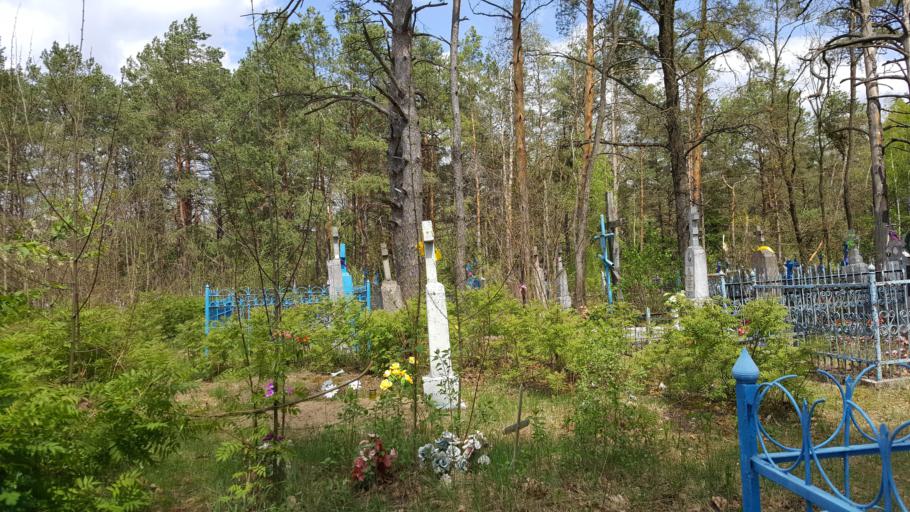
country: BY
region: Brest
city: Zhabinka
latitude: 52.4093
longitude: 24.0919
